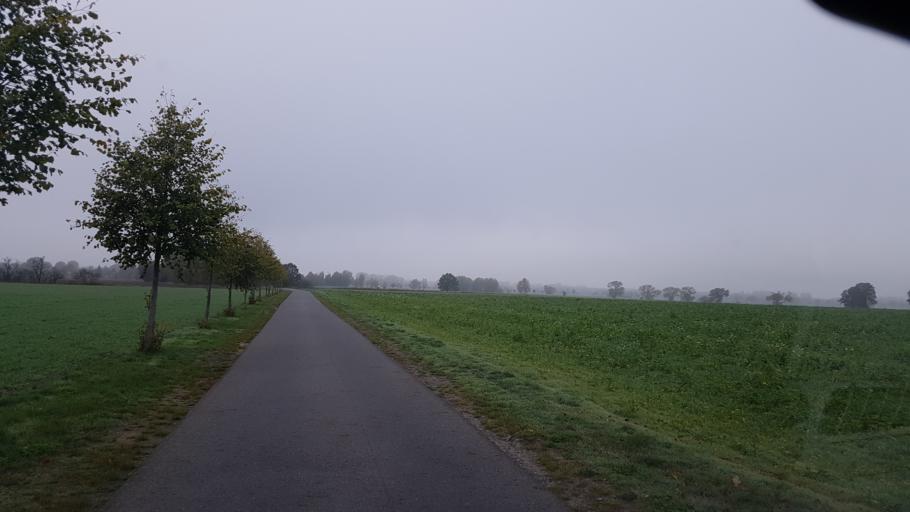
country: DE
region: Brandenburg
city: Schonewalde
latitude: 51.6773
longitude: 13.6211
